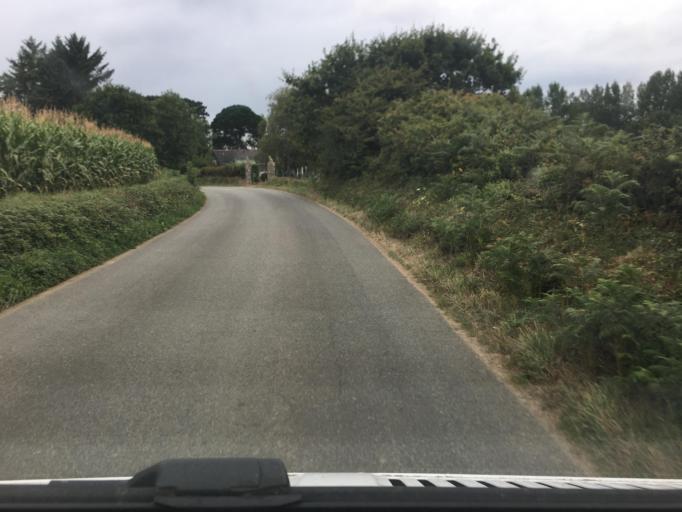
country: FR
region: Brittany
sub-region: Departement du Finistere
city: Beuzec-Cap-Sizun
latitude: 48.0776
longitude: -4.4760
